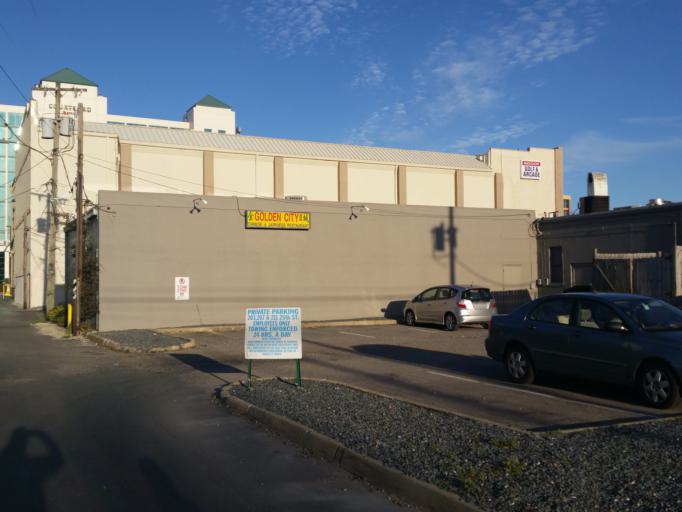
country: US
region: Virginia
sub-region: City of Virginia Beach
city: Virginia Beach
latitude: 36.8539
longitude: -75.9777
